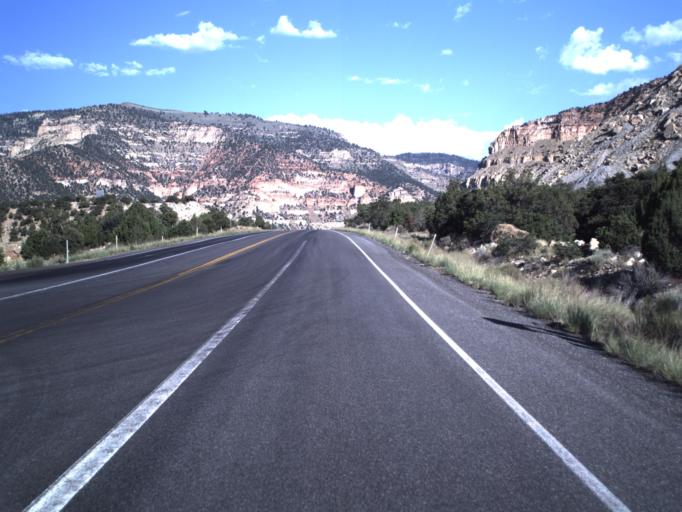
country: US
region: Utah
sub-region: Emery County
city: Huntington
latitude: 39.3874
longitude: -111.0828
